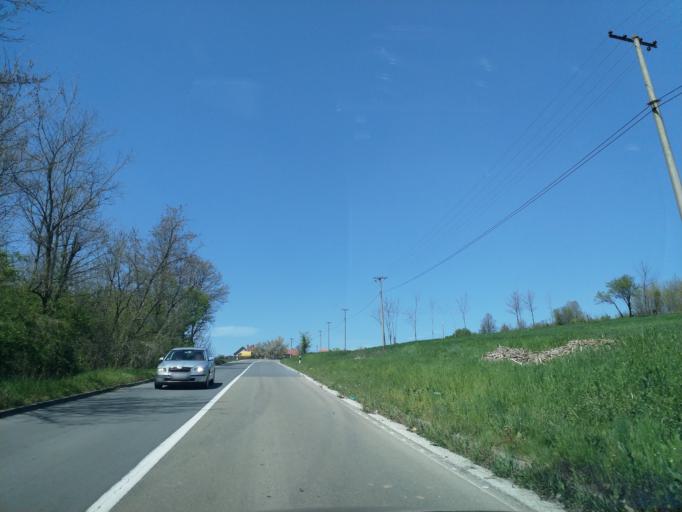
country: RS
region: Central Serbia
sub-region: Belgrade
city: Lazarevac
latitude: 44.3623
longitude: 20.3503
